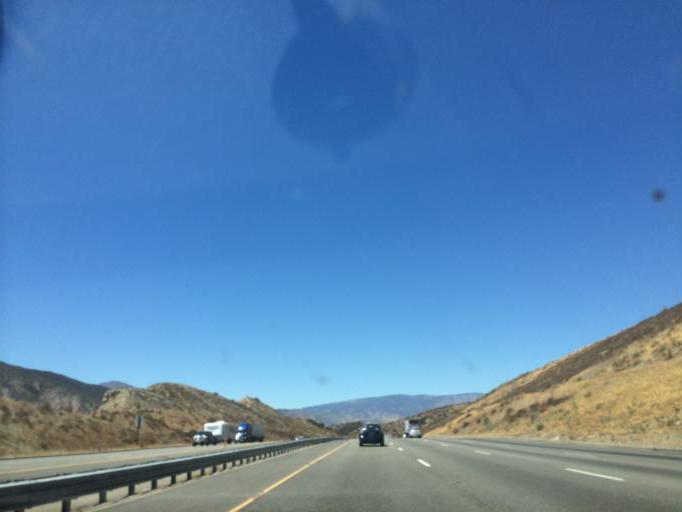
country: US
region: California
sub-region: Los Angeles County
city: Castaic
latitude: 34.6369
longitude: -118.7428
